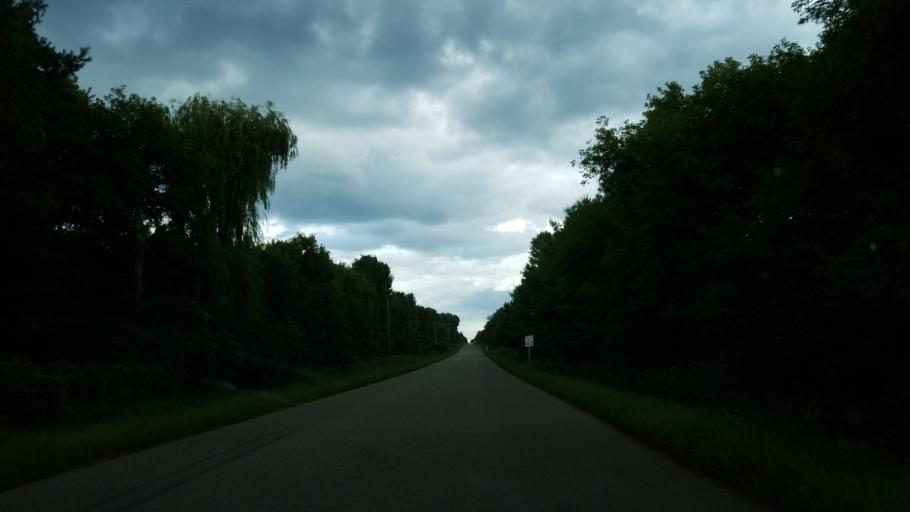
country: US
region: Minnesota
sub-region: Washington County
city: Afton
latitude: 44.8803
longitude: -92.7524
